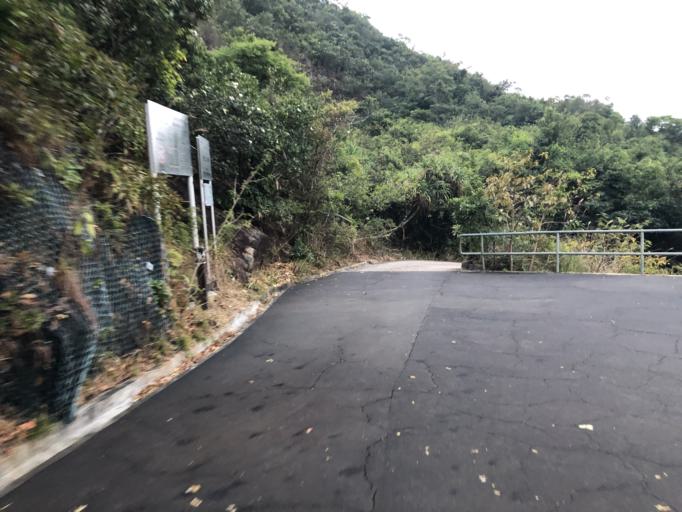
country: HK
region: Wanchai
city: Wan Chai
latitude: 22.2586
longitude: 114.2122
